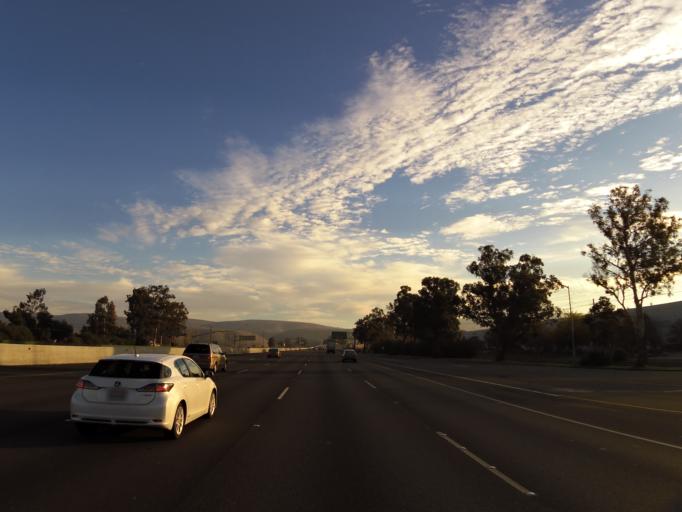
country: US
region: California
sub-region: Alameda County
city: Livermore
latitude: 37.7136
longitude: -121.7127
